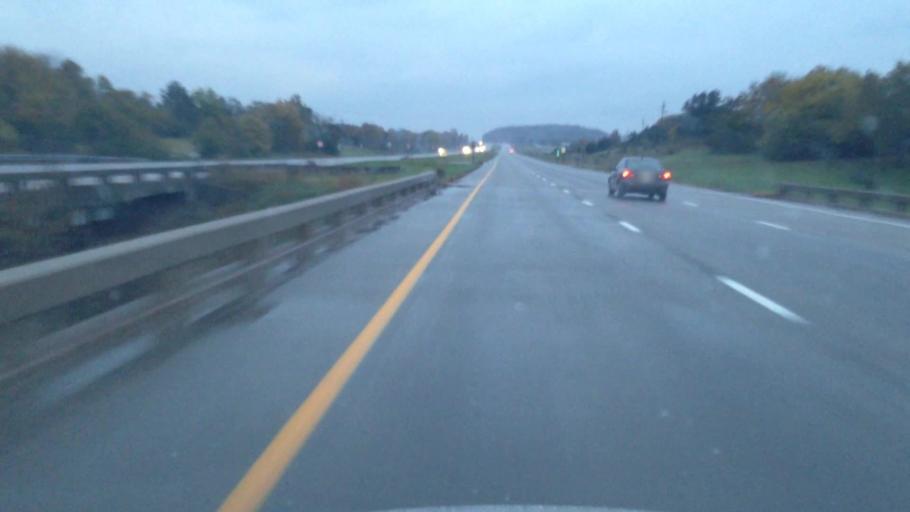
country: US
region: Kansas
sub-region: Douglas County
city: Lawrence
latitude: 38.9079
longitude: -95.2608
